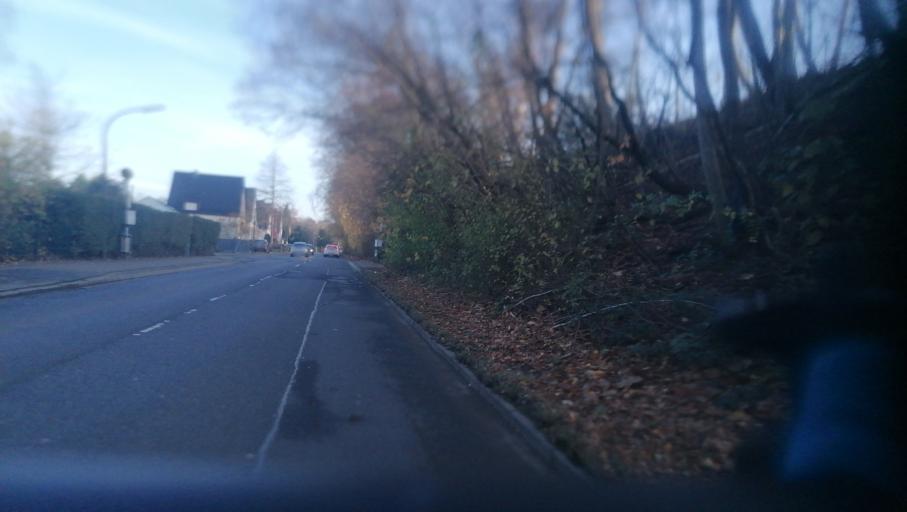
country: DE
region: North Rhine-Westphalia
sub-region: Regierungsbezirk Arnsberg
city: Dortmund
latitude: 51.4756
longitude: 7.4838
